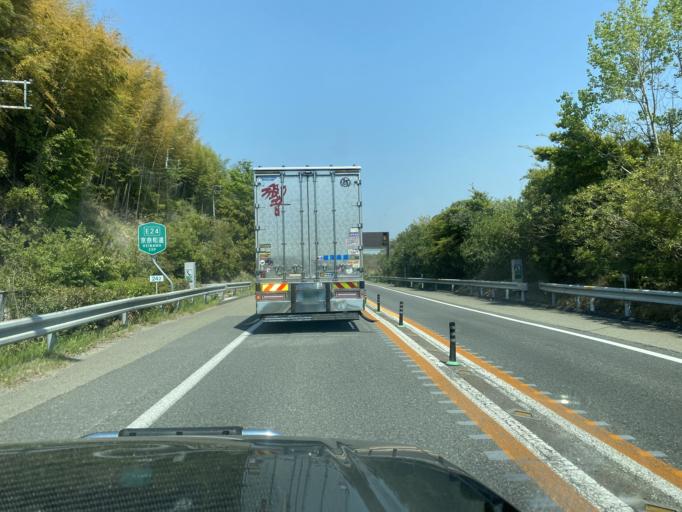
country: JP
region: Kyoto
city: Tanabe
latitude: 34.8103
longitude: 135.7540
